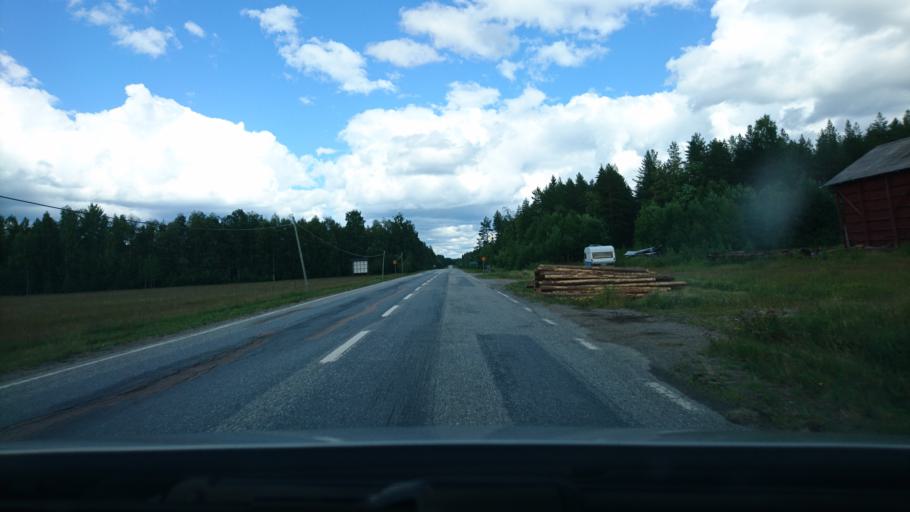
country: SE
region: Vaesternorrland
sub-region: Solleftea Kommun
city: As
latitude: 63.6960
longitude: 16.8939
